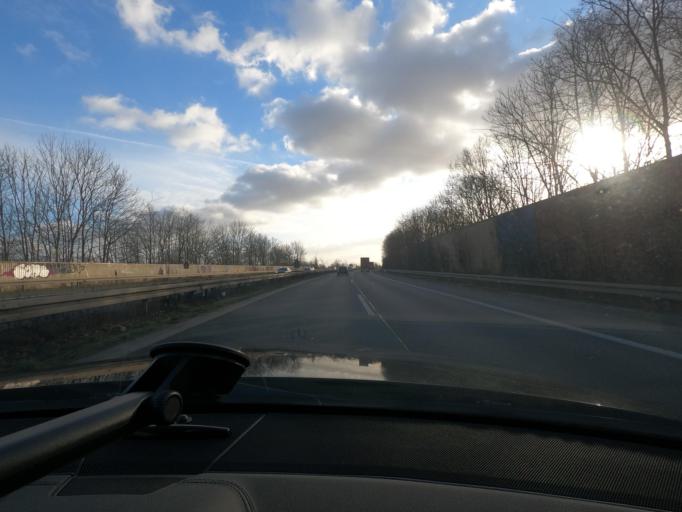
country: DE
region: North Rhine-Westphalia
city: Lanstrop
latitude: 51.5538
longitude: 7.5158
